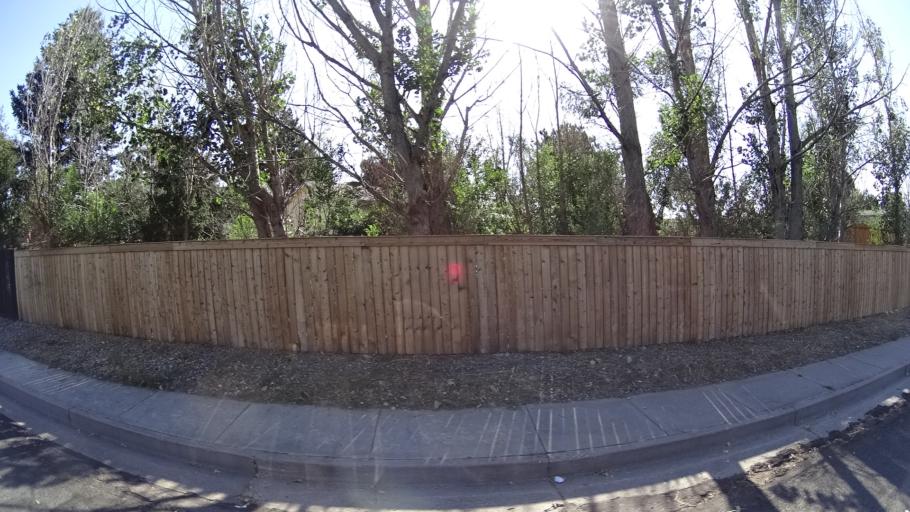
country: US
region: Colorado
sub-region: El Paso County
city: Cimarron Hills
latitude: 38.8809
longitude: -104.7228
